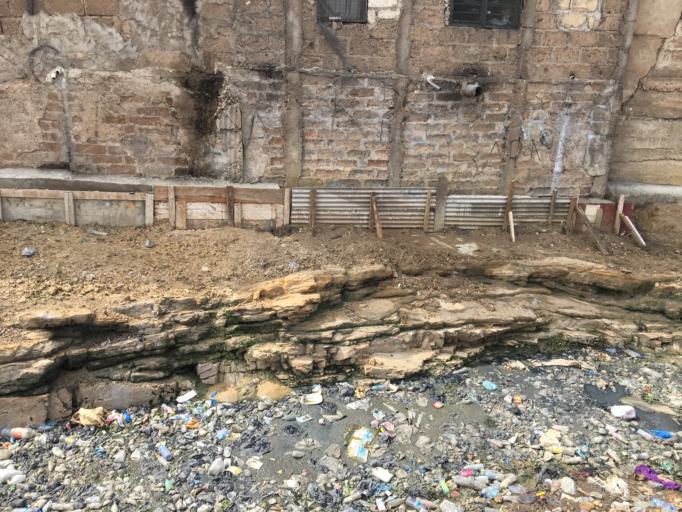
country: GH
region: Greater Accra
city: Accra
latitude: 5.5889
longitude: -0.1937
